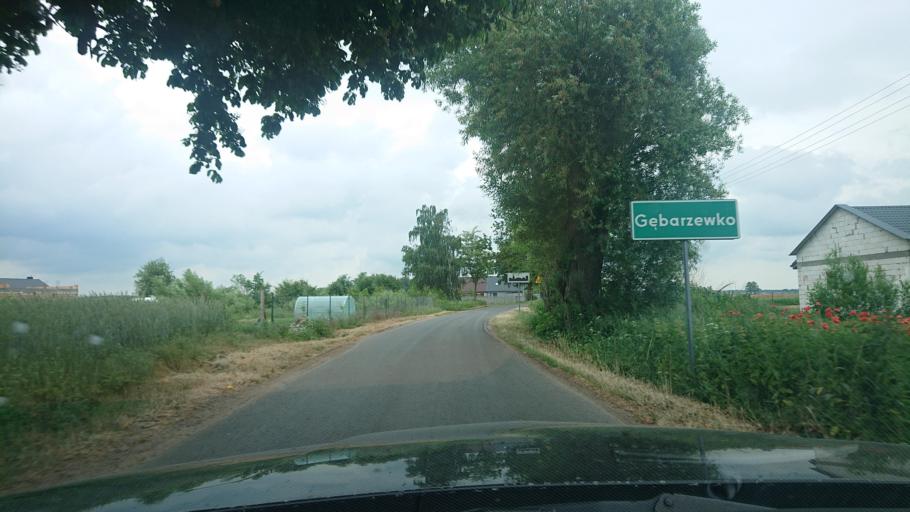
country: PL
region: Greater Poland Voivodeship
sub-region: Powiat gnieznienski
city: Gniezno
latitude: 52.4806
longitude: 17.5418
